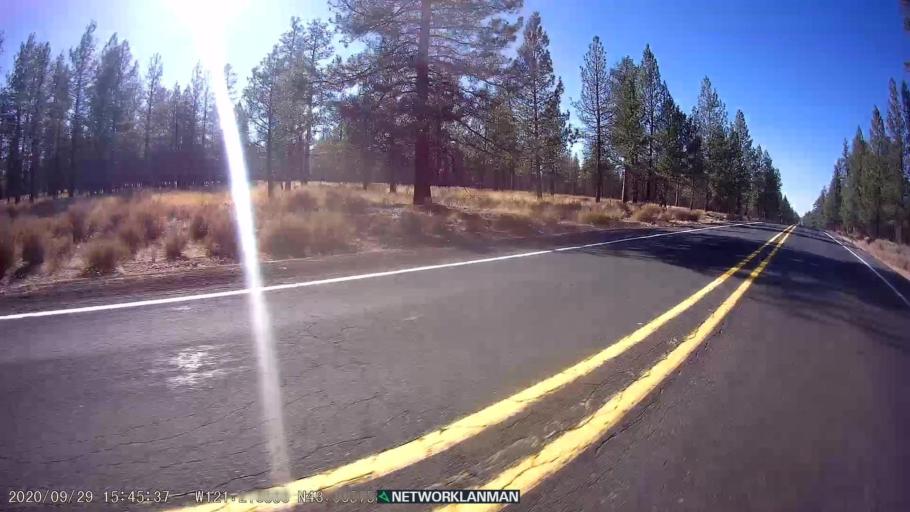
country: US
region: Oregon
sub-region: Deschutes County
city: La Pine
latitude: 43.3857
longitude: -121.2168
